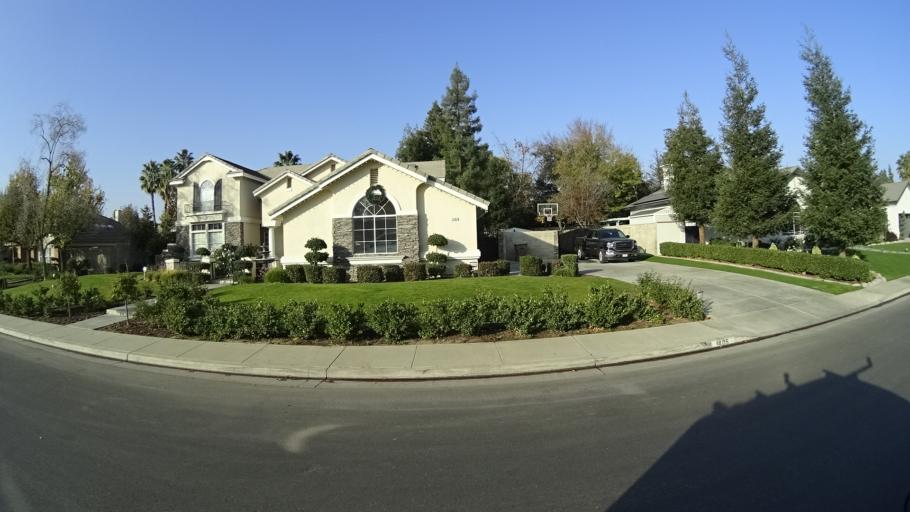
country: US
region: California
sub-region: Kern County
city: Rosedale
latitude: 35.3715
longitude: -119.1411
